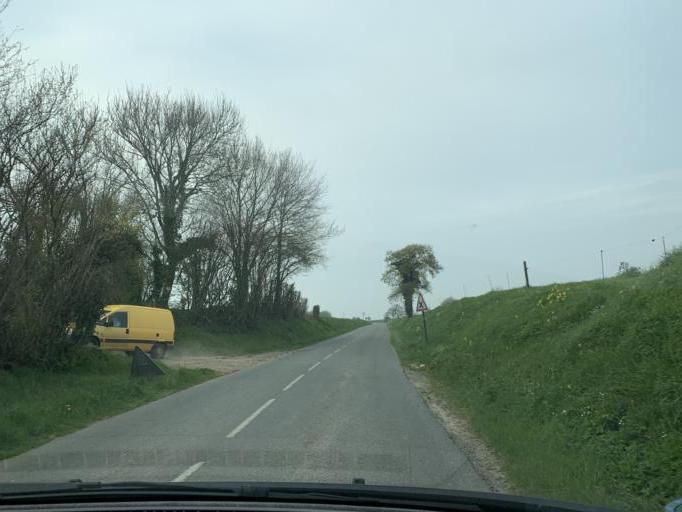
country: FR
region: Nord-Pas-de-Calais
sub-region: Departement du Pas-de-Calais
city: Longfosse
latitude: 50.7044
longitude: 1.7828
